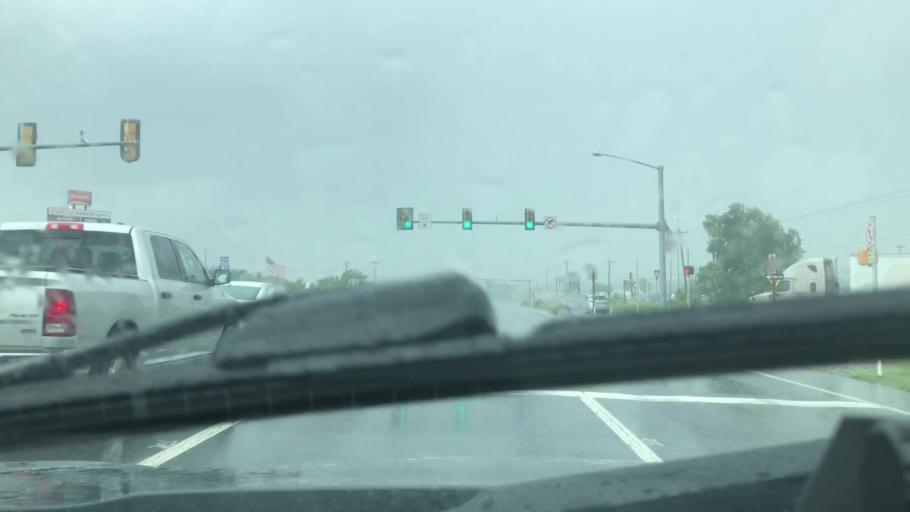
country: US
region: Pennsylvania
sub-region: Dauphin County
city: Skyline View
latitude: 40.3530
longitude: -76.7224
